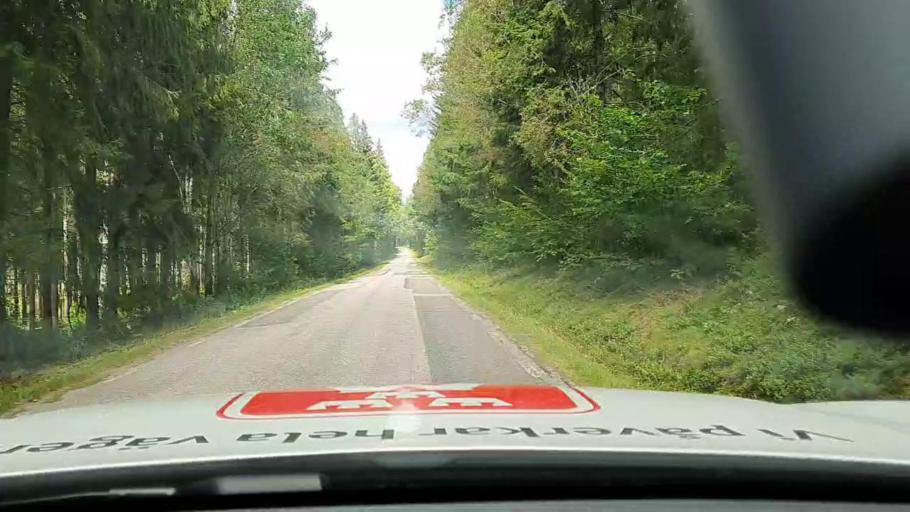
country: SE
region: Vaestra Goetaland
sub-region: Karlsborgs Kommun
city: Molltorp
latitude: 58.5769
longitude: 14.2665
